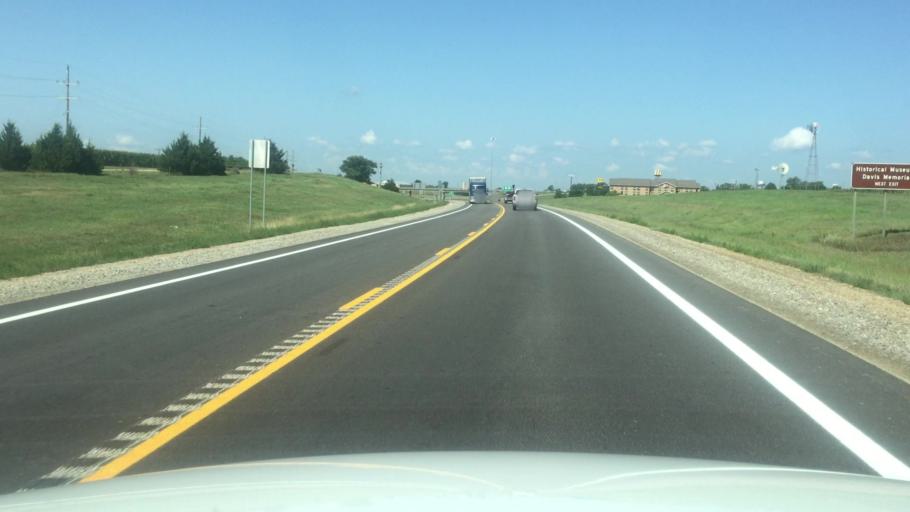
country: US
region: Kansas
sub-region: Brown County
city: Hiawatha
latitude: 39.8421
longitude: -95.5188
